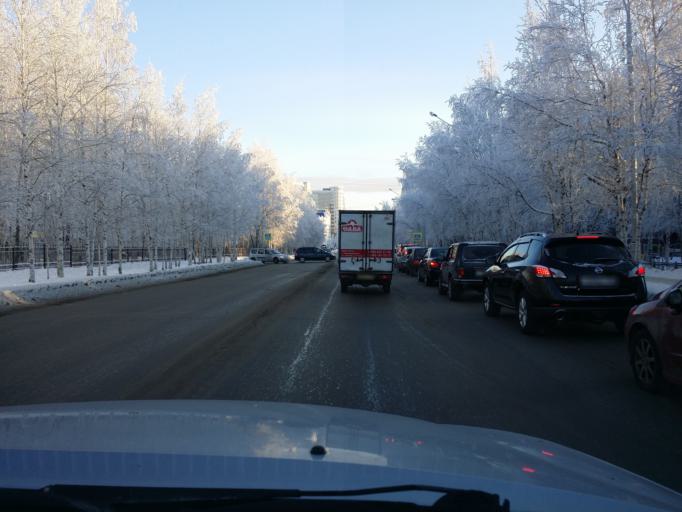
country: RU
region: Khanty-Mansiyskiy Avtonomnyy Okrug
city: Nizhnevartovsk
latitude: 60.9372
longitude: 76.5697
